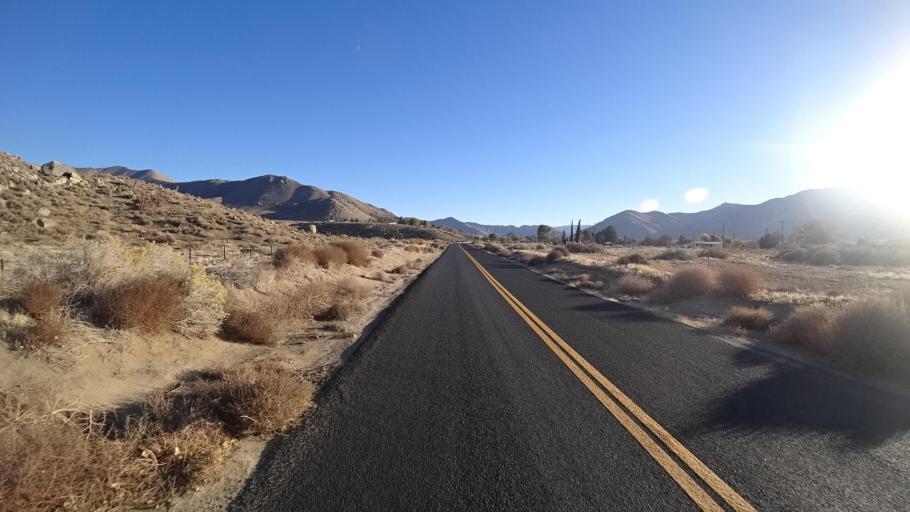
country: US
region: California
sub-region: Kern County
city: Weldon
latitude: 35.6450
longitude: -118.2502
